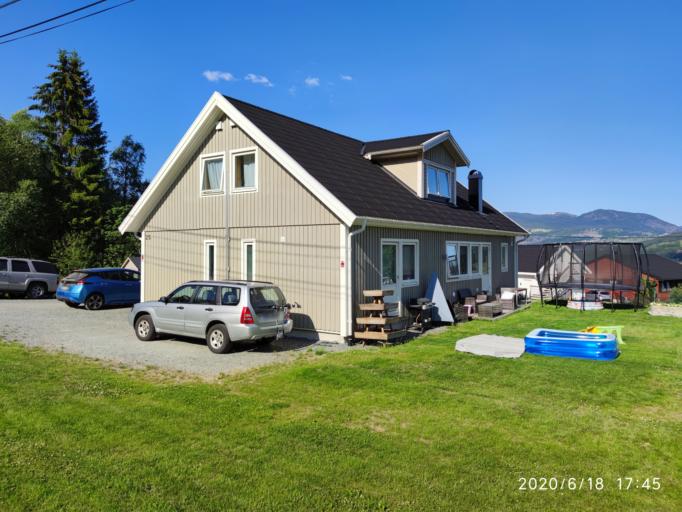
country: NO
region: Hordaland
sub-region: Voss
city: Voss
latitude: 60.6593
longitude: 6.4216
